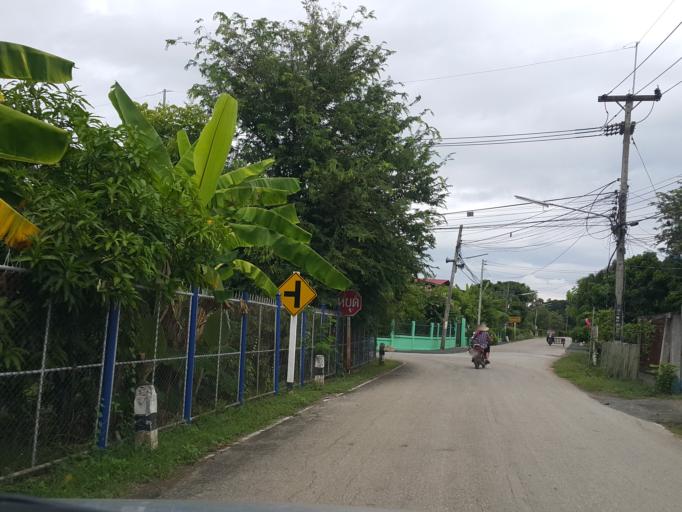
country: TH
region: Chiang Mai
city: San Kamphaeng
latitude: 18.7954
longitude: 99.1384
